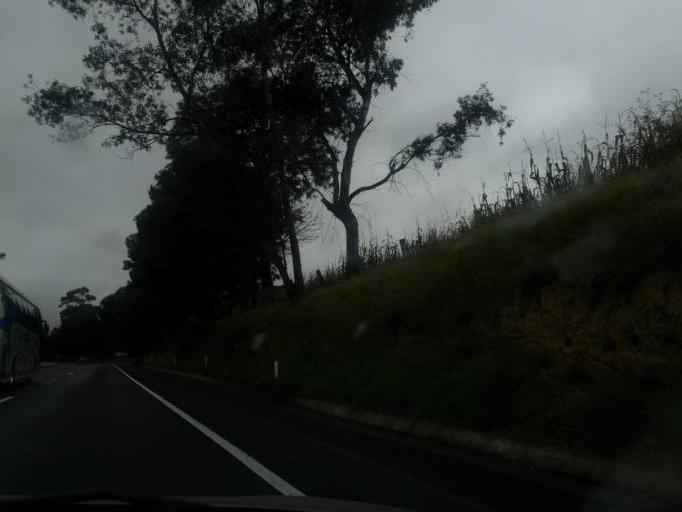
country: MX
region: Mexico City
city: Xochimilco
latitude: 19.1815
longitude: -99.1556
